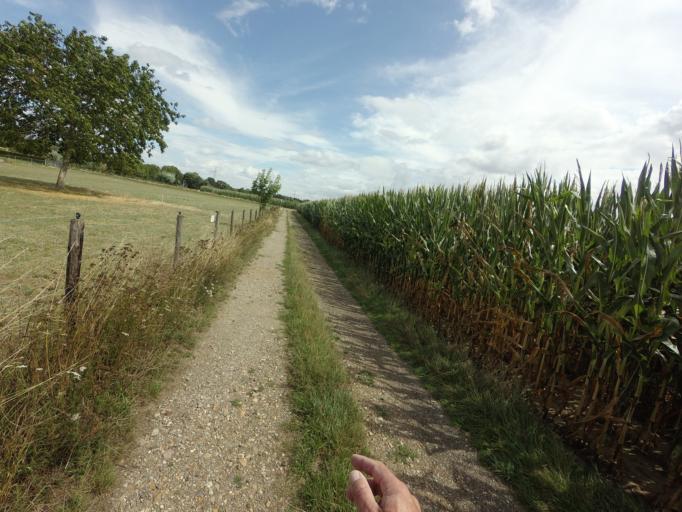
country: BE
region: Flanders
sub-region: Provincie Limburg
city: Maaseik
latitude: 51.1174
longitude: 5.8208
